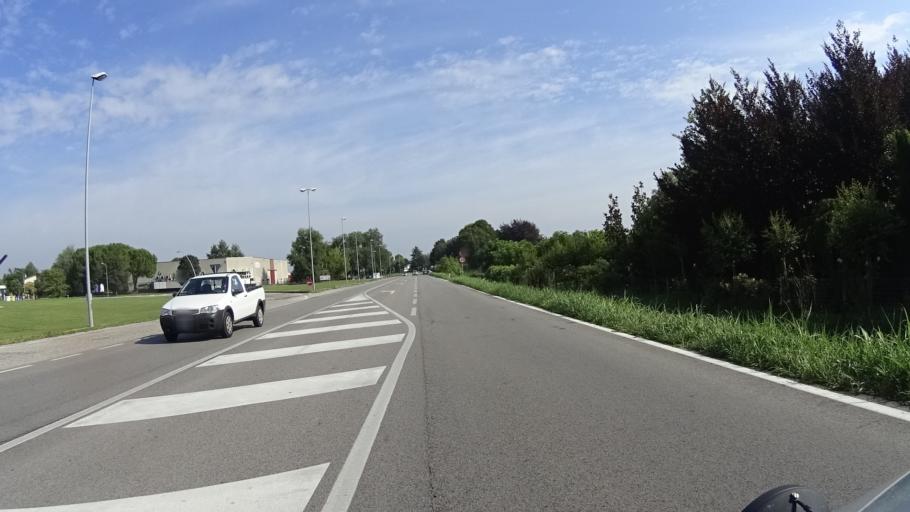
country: IT
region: Veneto
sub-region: Provincia di Venezia
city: San Michele al Tagliamento
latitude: 45.7669
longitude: 12.9850
